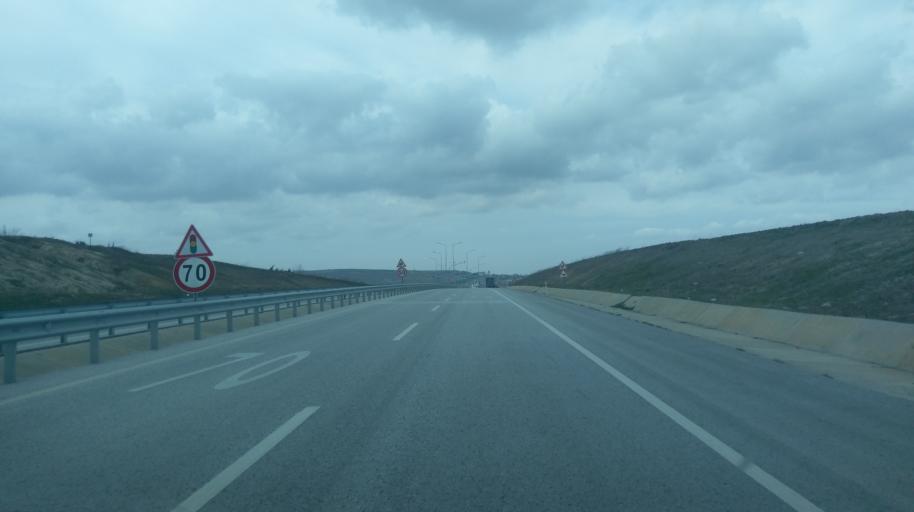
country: TR
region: Edirne
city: Uzun Keupru
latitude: 41.2720
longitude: 26.7098
